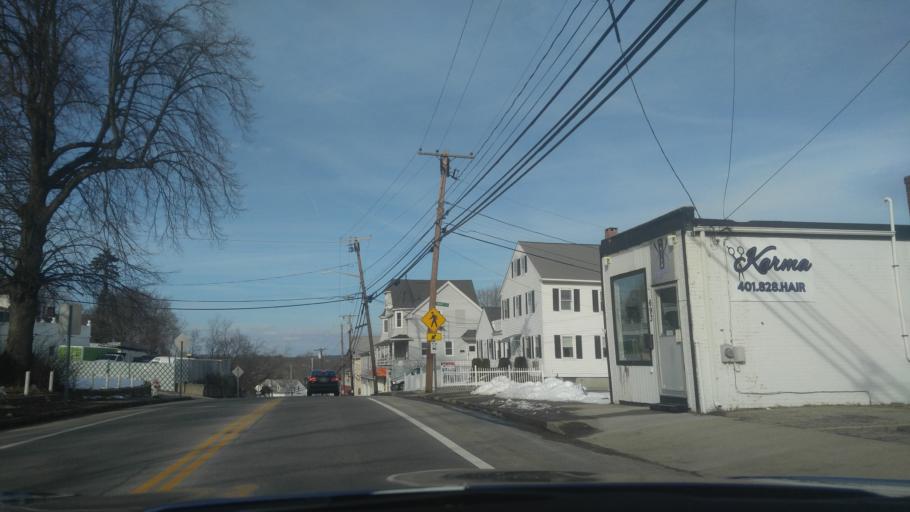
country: US
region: Rhode Island
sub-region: Kent County
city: West Warwick
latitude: 41.7191
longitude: -71.4919
